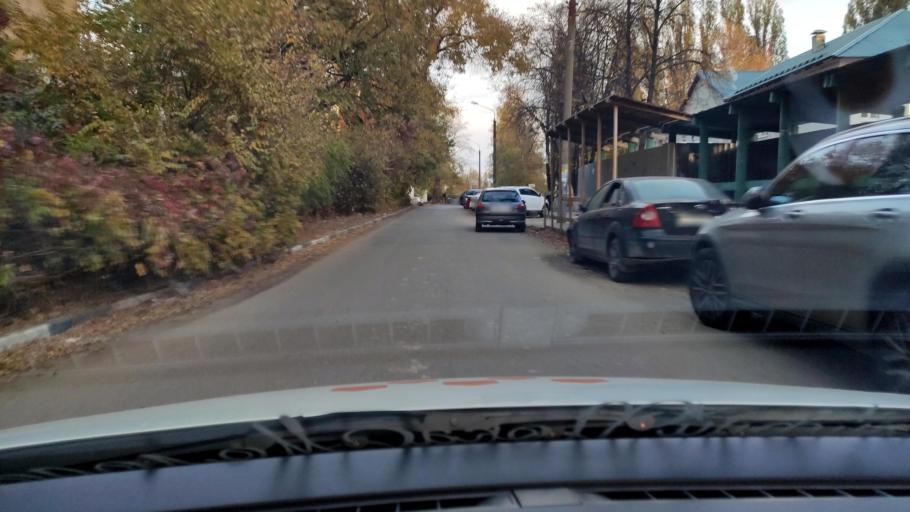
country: RU
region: Voronezj
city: Voronezh
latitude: 51.6971
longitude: 39.1840
